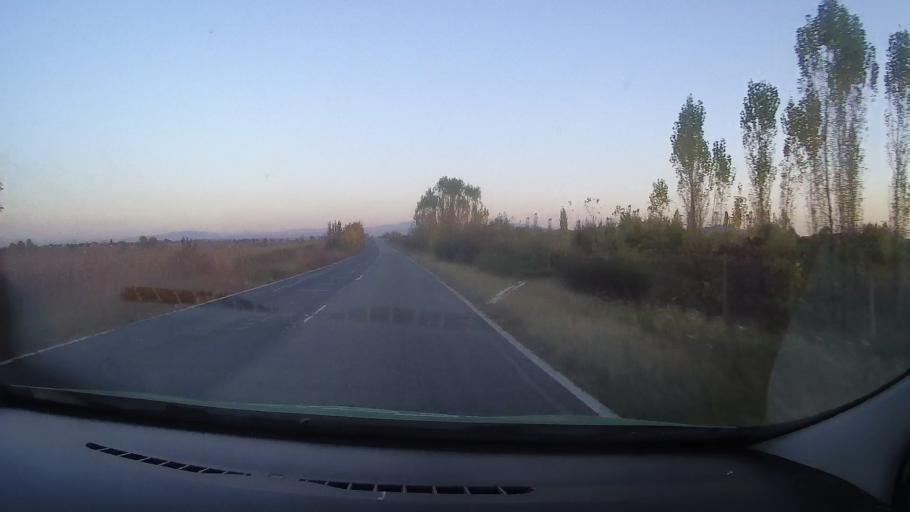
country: RO
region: Timis
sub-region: Comuna Dumbrava
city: Rachita
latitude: 45.8232
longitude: 22.0959
